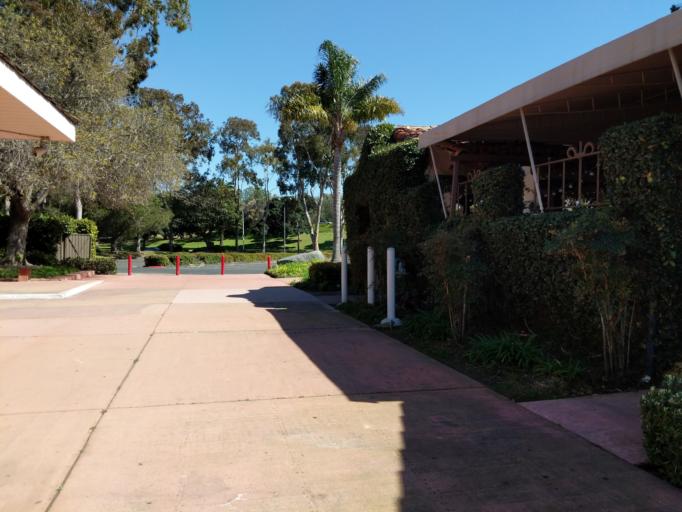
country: US
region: California
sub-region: San Diego County
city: San Diego
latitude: 32.7608
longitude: -117.2340
